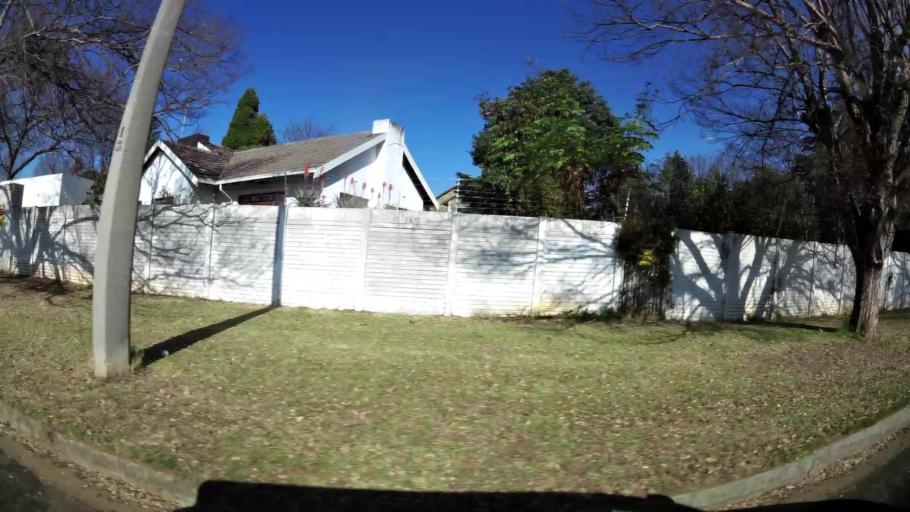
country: ZA
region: Gauteng
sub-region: Ekurhuleni Metropolitan Municipality
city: Benoni
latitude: -26.1377
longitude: 28.3429
